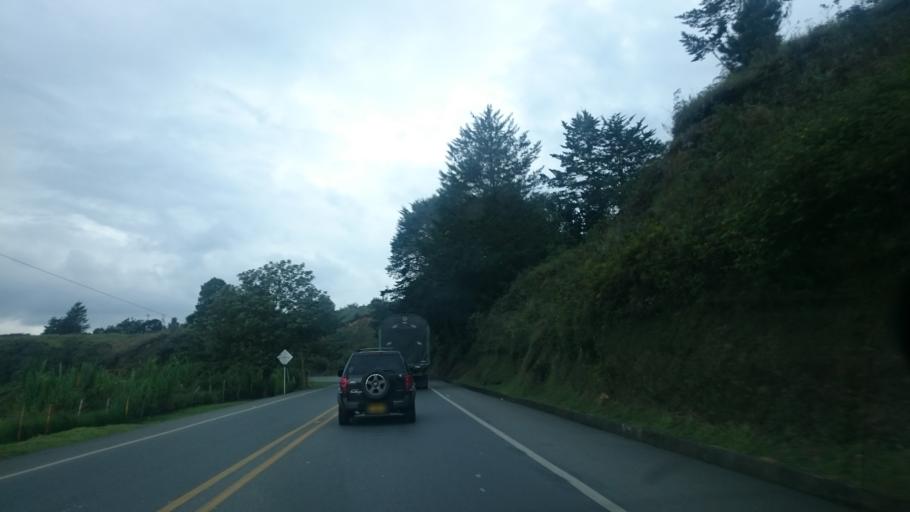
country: CO
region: Cauca
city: Cajibio
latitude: 2.5514
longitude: -76.5667
